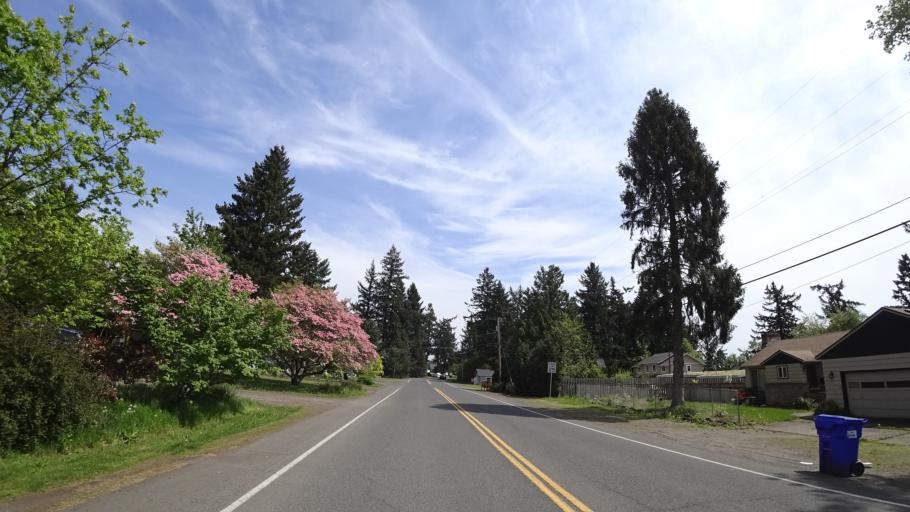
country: US
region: Oregon
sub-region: Clackamas County
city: Milwaukie
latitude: 45.4647
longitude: -122.6058
